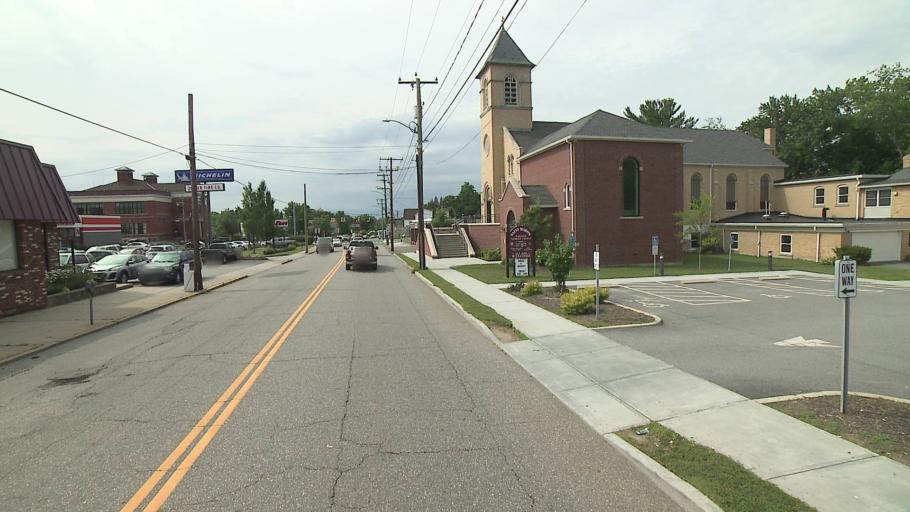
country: US
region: Connecticut
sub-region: Litchfield County
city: Torrington
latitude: 41.8132
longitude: -73.1214
